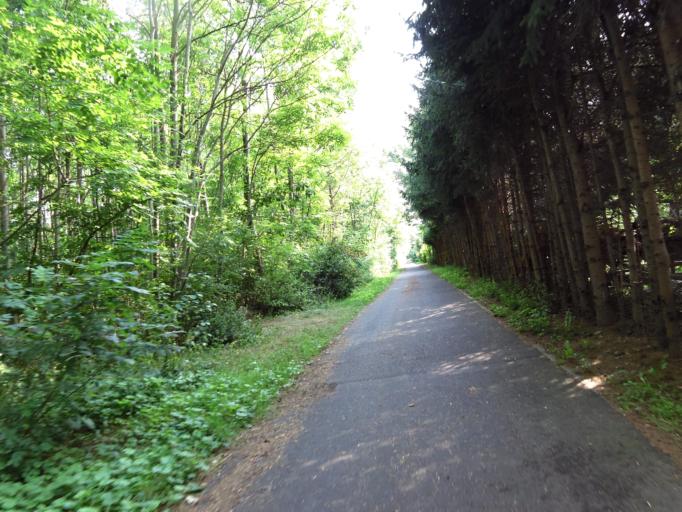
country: DE
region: Saxony
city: Leipzig
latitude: 51.3851
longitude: 12.3879
